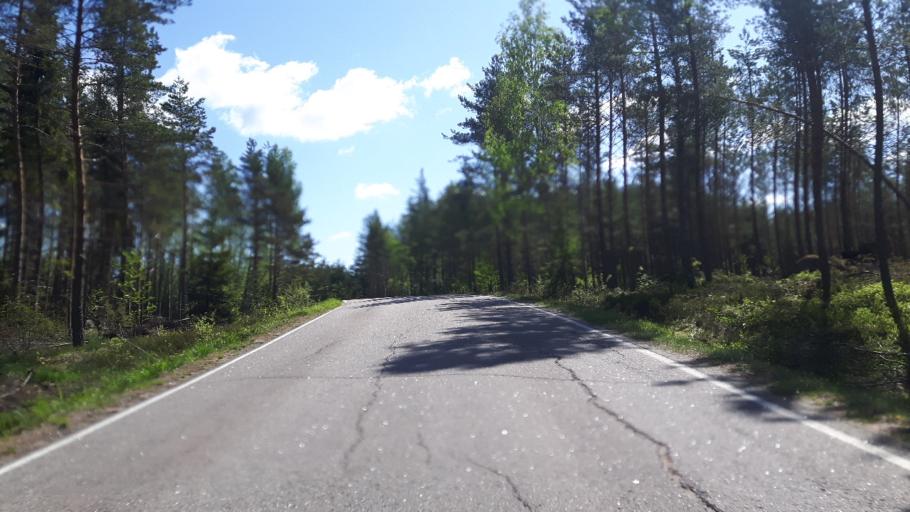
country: FI
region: Kymenlaakso
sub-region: Kotka-Hamina
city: Hamina
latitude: 60.5132
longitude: 27.3911
